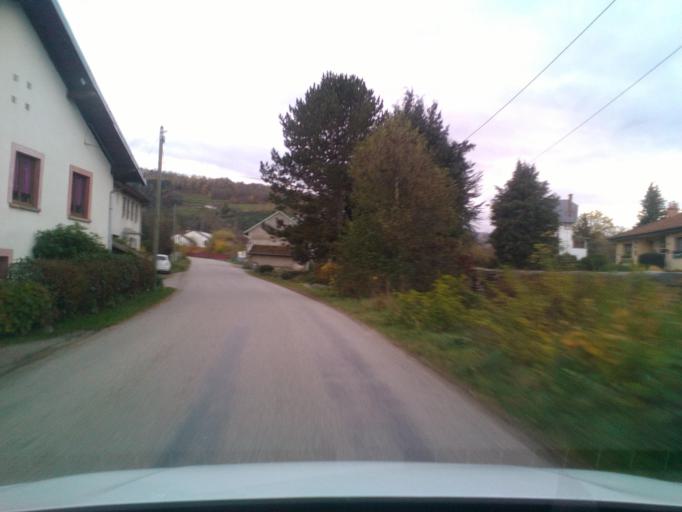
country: FR
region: Lorraine
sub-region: Departement des Vosges
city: Ban-de-Laveline
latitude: 48.2349
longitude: 7.0607
